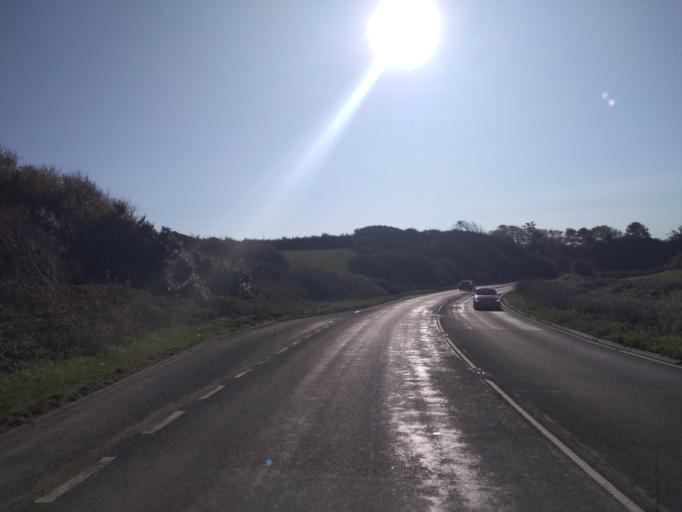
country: GB
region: England
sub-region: East Sussex
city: Newhaven
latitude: 50.7929
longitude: 0.0694
